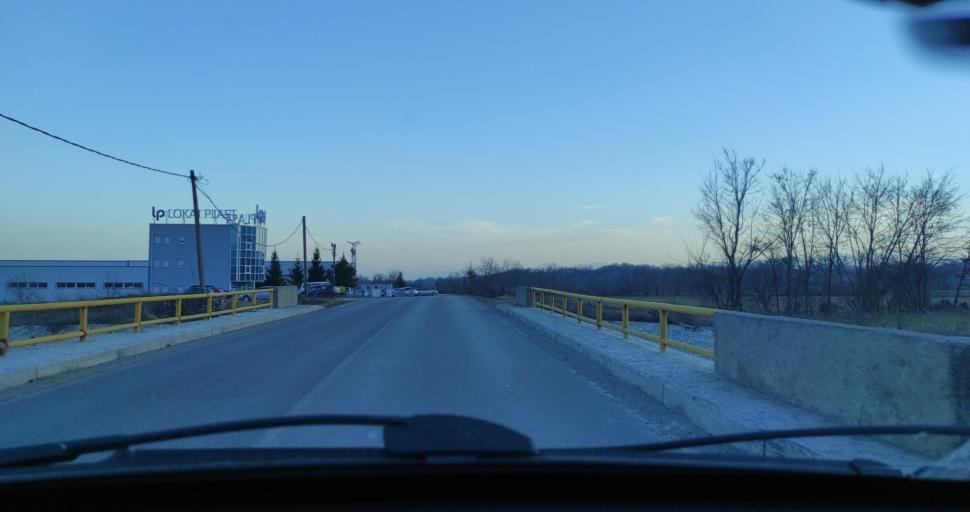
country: XK
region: Gjakova
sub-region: Komuna e Decanit
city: Dranoc
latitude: 42.5185
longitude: 20.3058
